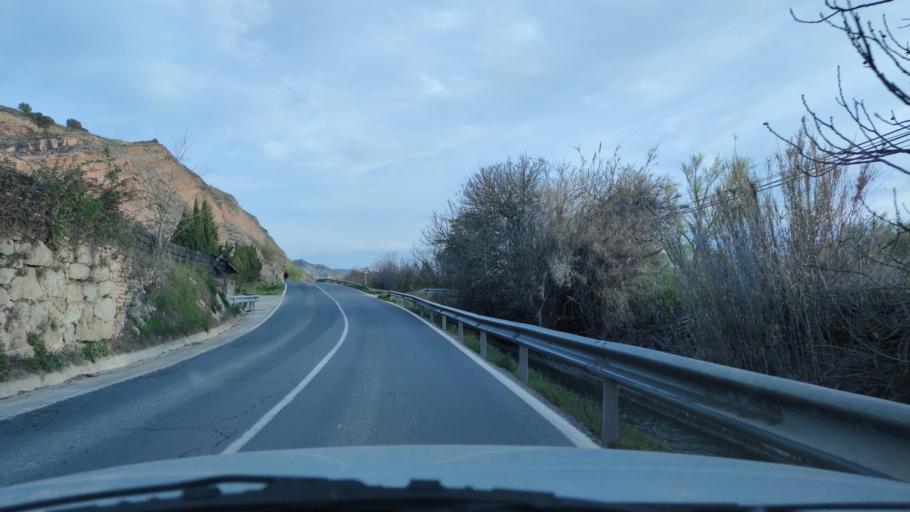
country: ES
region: Catalonia
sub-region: Provincia de Lleida
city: Balaguer
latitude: 41.8032
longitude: 0.8087
